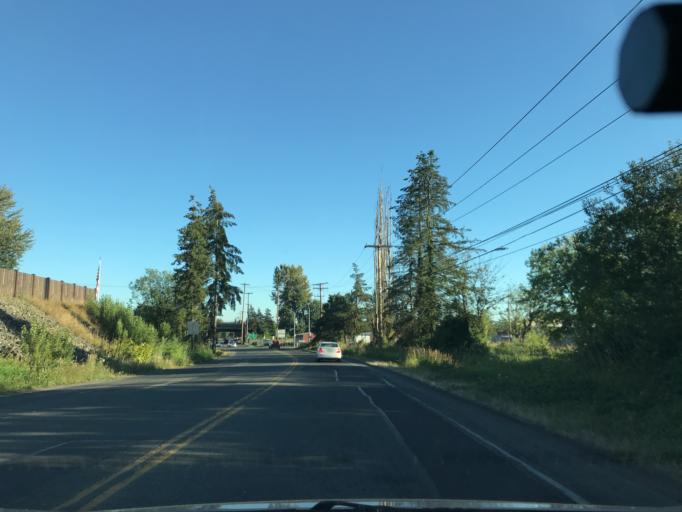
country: US
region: Washington
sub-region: Pierce County
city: Bonney Lake
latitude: 47.2004
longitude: -122.2082
